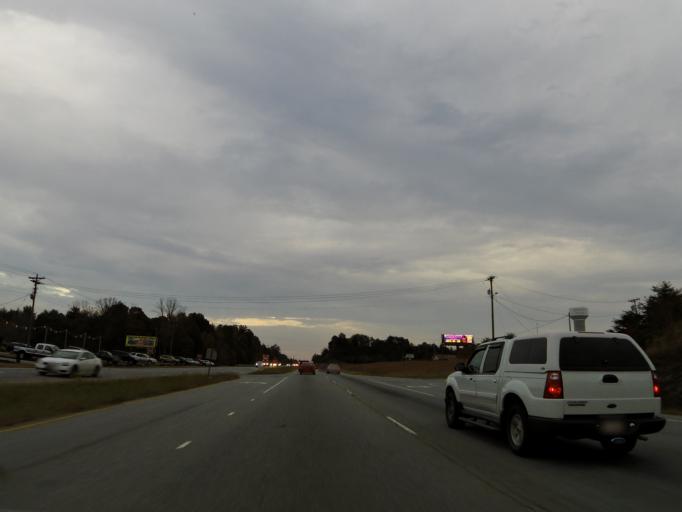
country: US
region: North Carolina
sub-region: Caldwell County
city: Granite Falls
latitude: 35.7857
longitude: -81.4059
